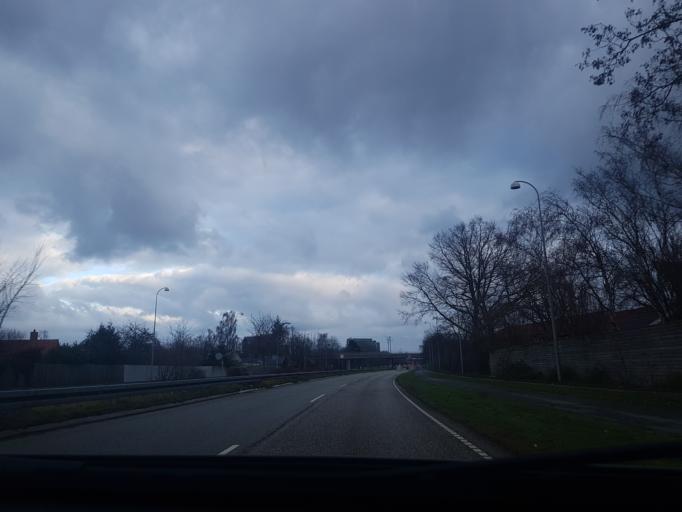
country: DK
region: Capital Region
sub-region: Vallensbaek Kommune
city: Vallensbaek
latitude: 55.6215
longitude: 12.3819
